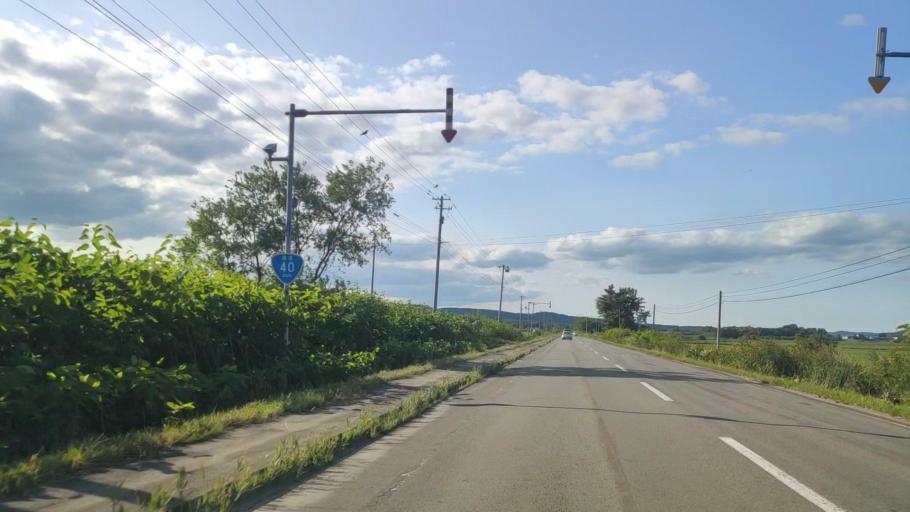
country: JP
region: Hokkaido
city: Makubetsu
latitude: 44.8260
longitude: 142.0632
